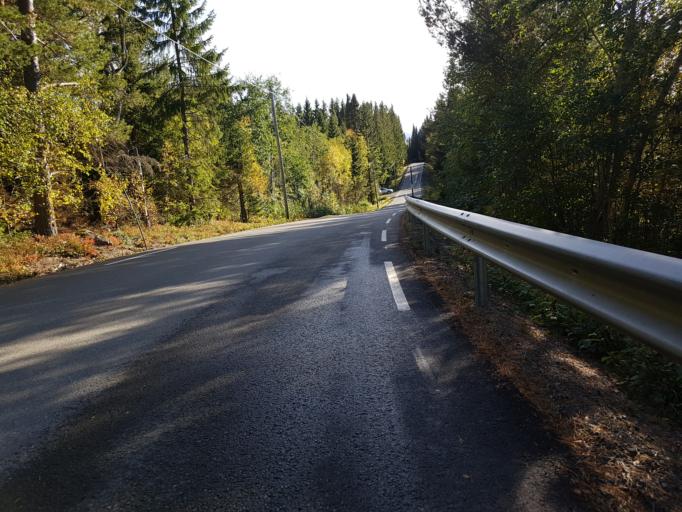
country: NO
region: Sor-Trondelag
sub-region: Malvik
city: Malvik
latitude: 63.3806
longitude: 10.6001
